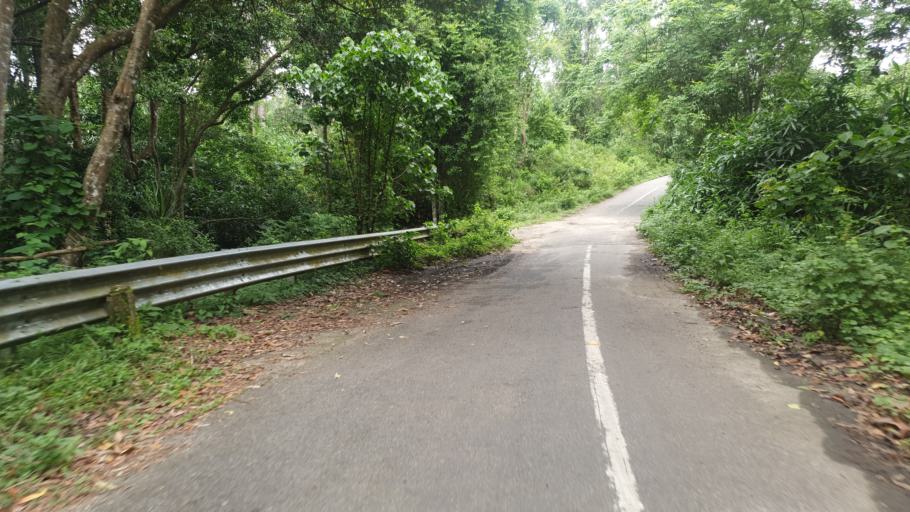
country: IN
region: Kerala
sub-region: Thiruvananthapuram
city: Nedumangad
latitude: 8.6423
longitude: 77.1102
